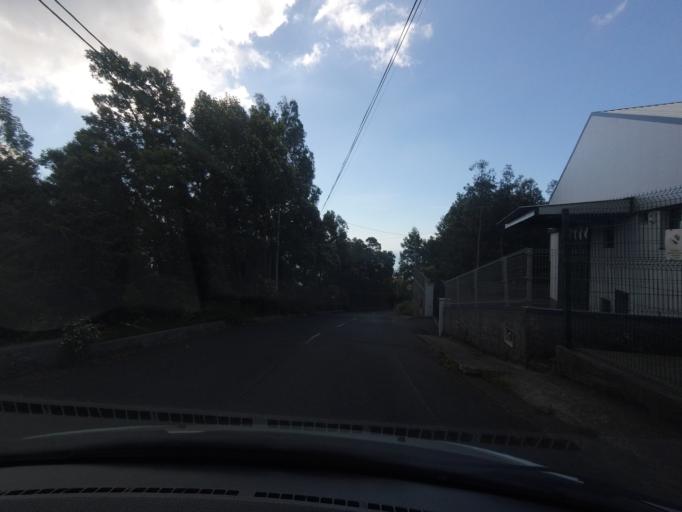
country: PT
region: Madeira
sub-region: Santa Cruz
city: Camacha
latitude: 32.6675
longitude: -16.8540
